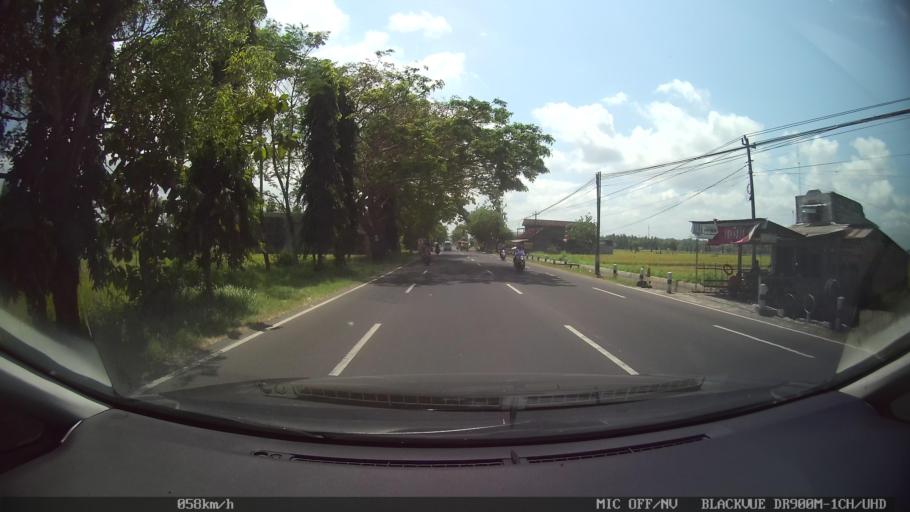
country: ID
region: Daerah Istimewa Yogyakarta
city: Pandak
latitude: -7.9237
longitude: 110.2800
